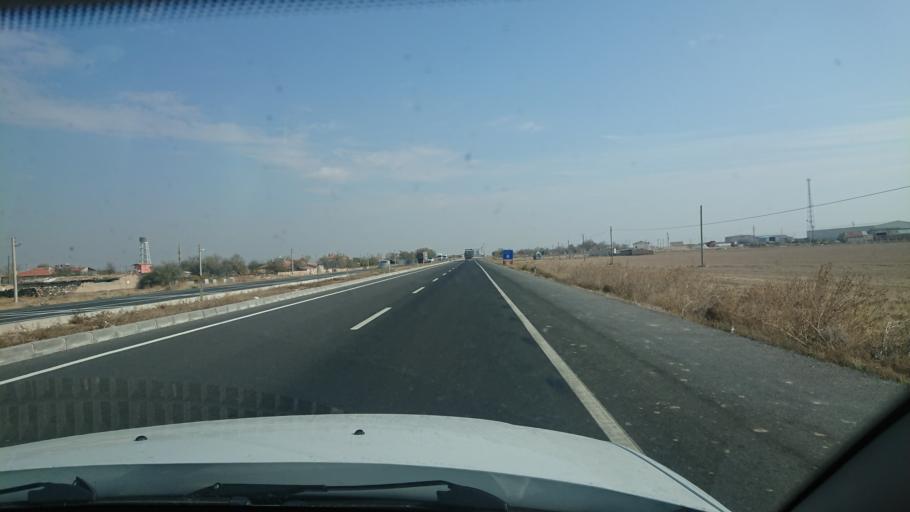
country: TR
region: Aksaray
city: Yesilova
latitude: 38.3234
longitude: 33.8768
